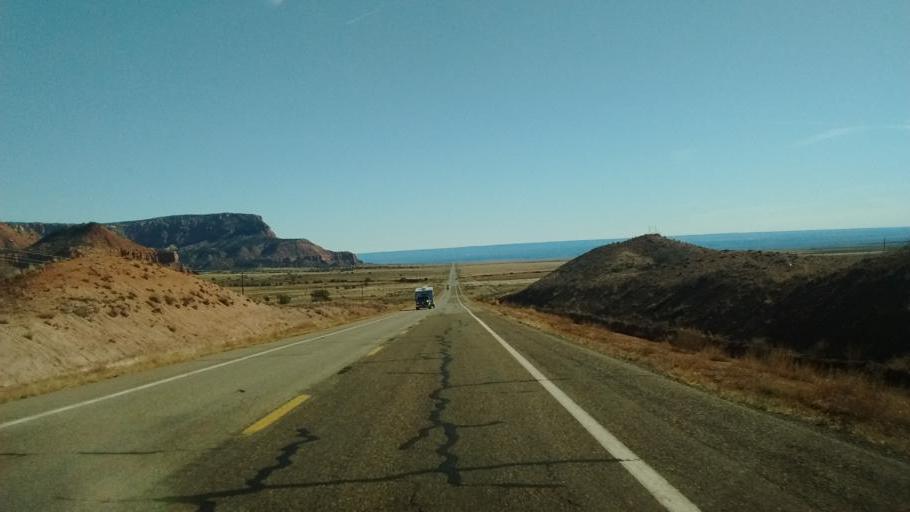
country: US
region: Arizona
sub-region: Mohave County
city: Colorado City
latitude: 36.8795
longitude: -112.8887
